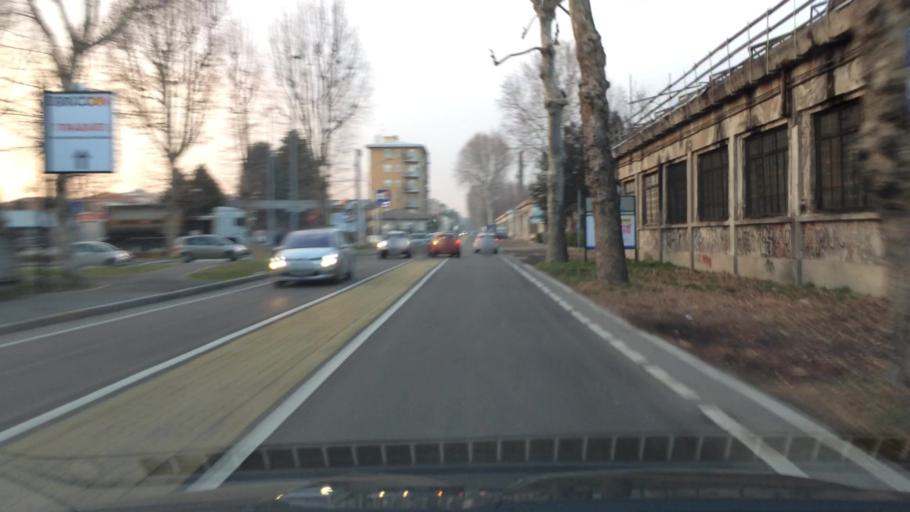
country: IT
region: Lombardy
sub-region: Provincia di Varese
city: Saronno
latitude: 45.6169
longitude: 9.0318
